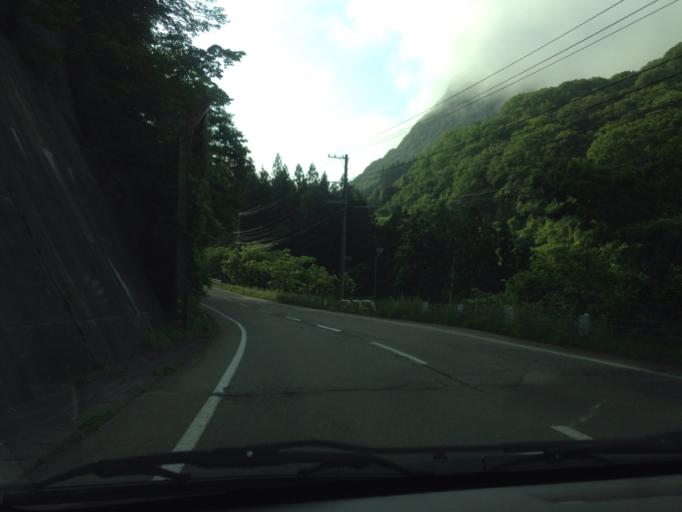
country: JP
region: Fukushima
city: Inawashiro
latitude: 37.3078
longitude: 139.9155
